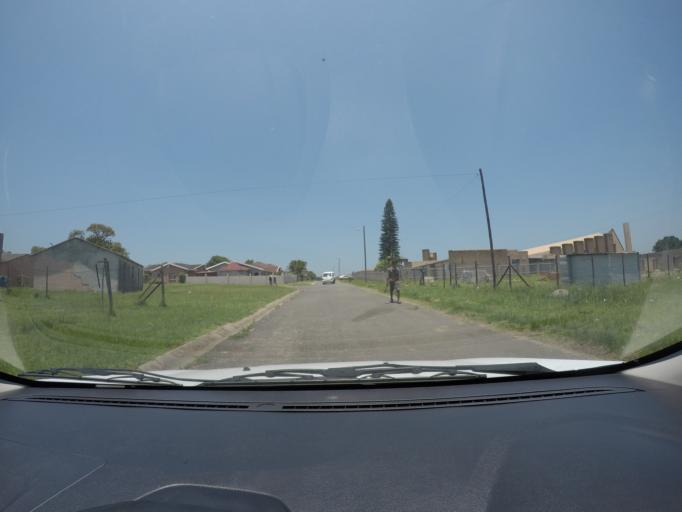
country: ZA
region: KwaZulu-Natal
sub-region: uThungulu District Municipality
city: eSikhawini
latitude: -28.8828
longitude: 31.8997
